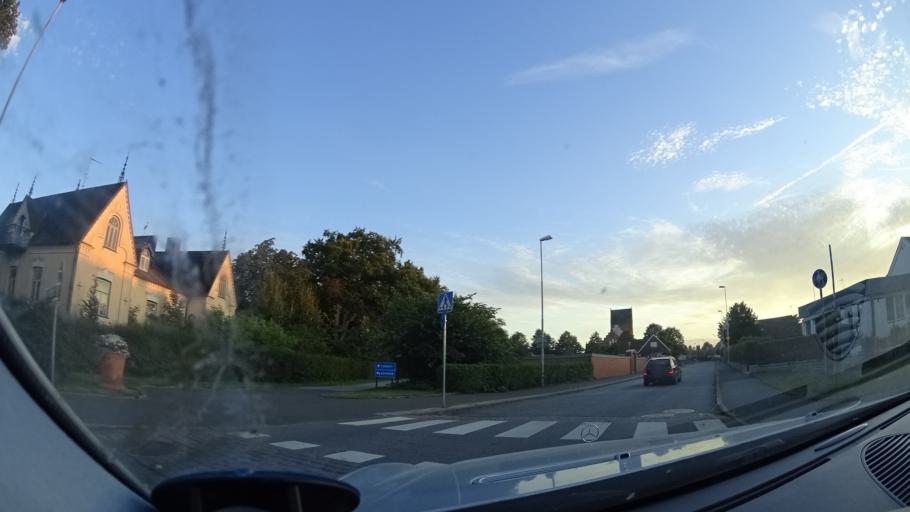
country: SE
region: Skane
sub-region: Kristianstads Kommun
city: Ahus
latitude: 55.9241
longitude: 14.2964
